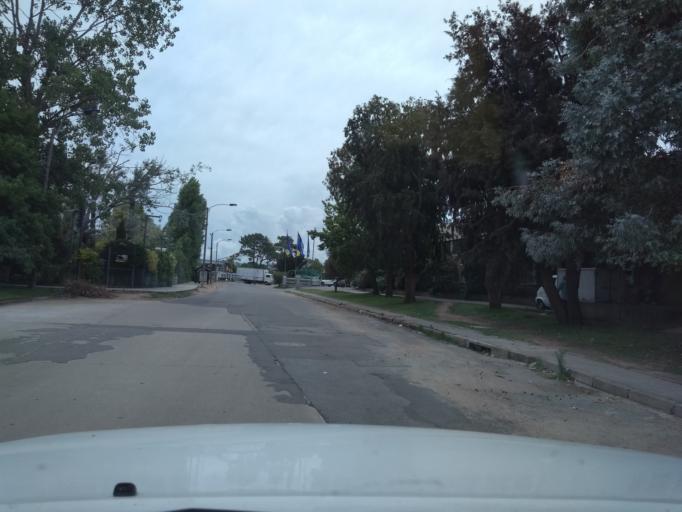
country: UY
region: Canelones
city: Paso de Carrasco
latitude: -34.8784
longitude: -56.0574
